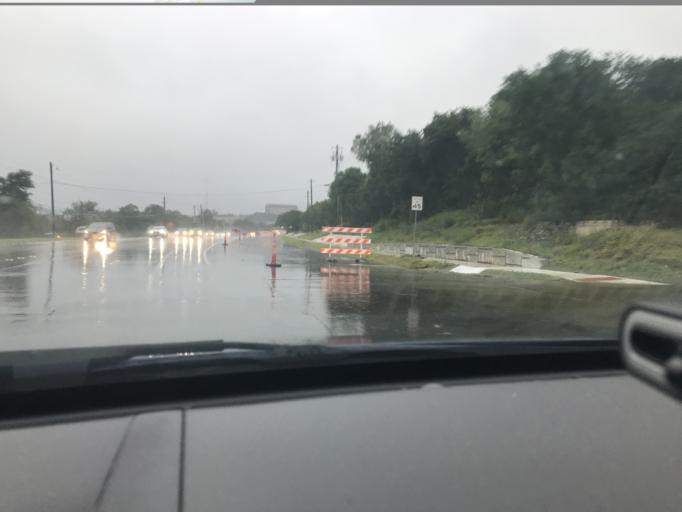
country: US
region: Texas
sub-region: Travis County
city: West Lake Hills
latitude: 30.2896
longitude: -97.8187
